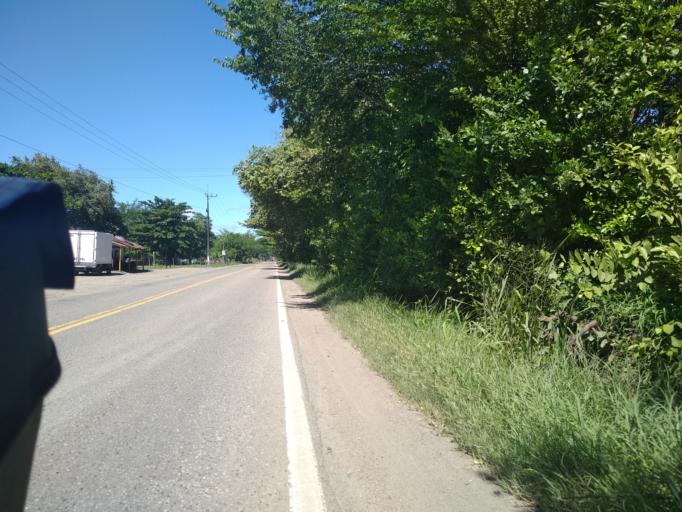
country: CO
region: Cundinamarca
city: Puerto Salgar
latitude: 5.4801
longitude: -74.6440
